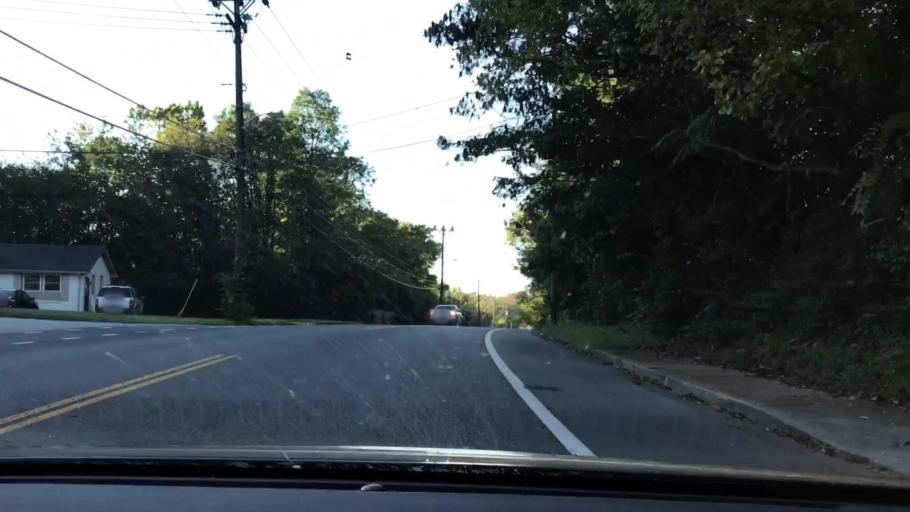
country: US
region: Tennessee
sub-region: Williamson County
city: Brentwood Estates
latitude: 36.0576
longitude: -86.7019
